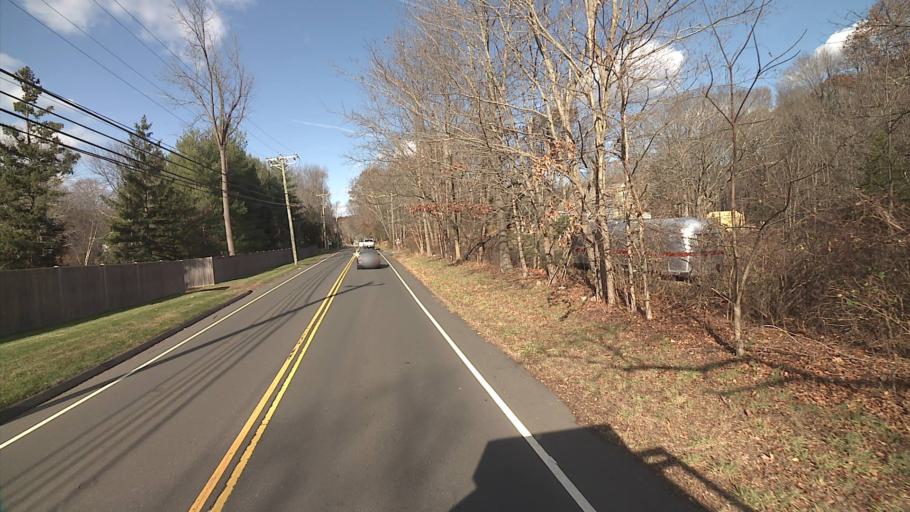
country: US
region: Connecticut
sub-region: Fairfield County
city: Georgetown
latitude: 41.2275
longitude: -73.3823
